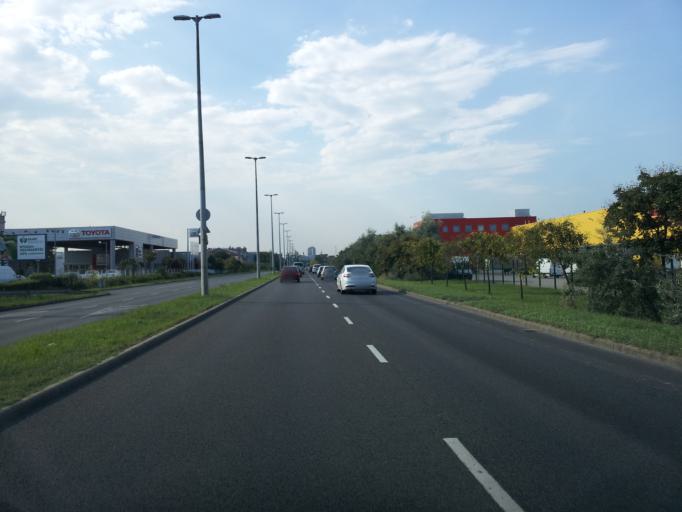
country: HU
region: Budapest
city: Budapest XX. keruelet
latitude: 47.4606
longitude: 19.1095
